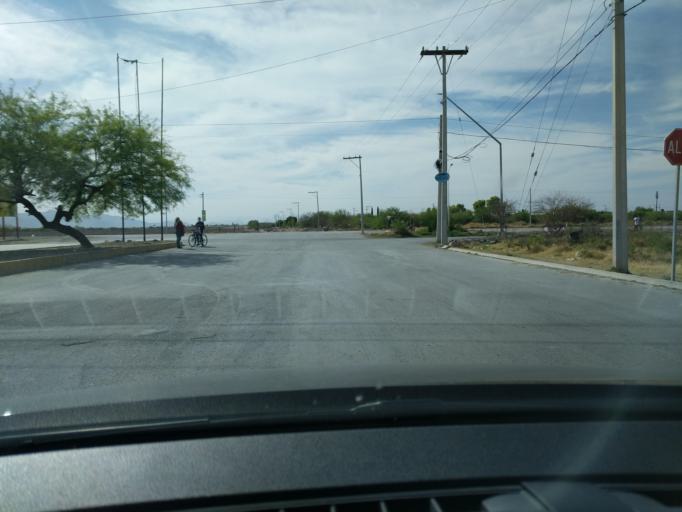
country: MX
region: Coahuila
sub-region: Torreon
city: Fraccionamiento la Noria
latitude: 25.5205
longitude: -103.3168
